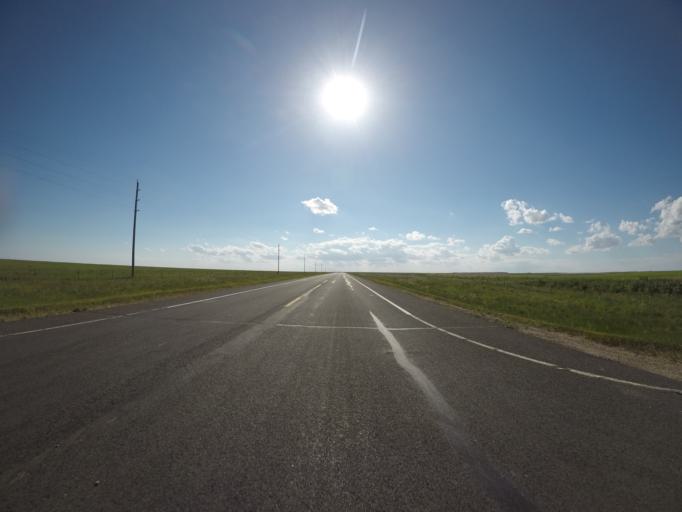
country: US
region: Colorado
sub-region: Morgan County
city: Fort Morgan
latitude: 40.6104
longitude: -103.7343
